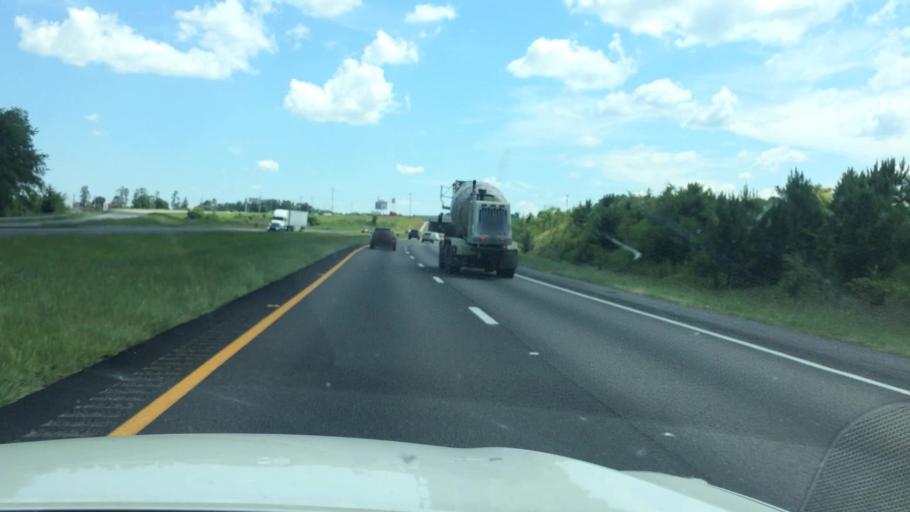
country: US
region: South Carolina
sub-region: Aiken County
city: Belvedere
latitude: 33.5623
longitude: -81.9404
